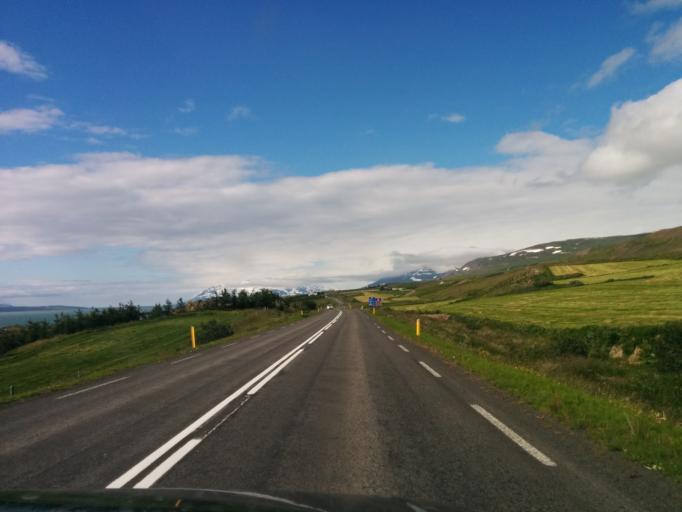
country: IS
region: Northeast
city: Akureyri
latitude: 65.7342
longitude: -18.0739
